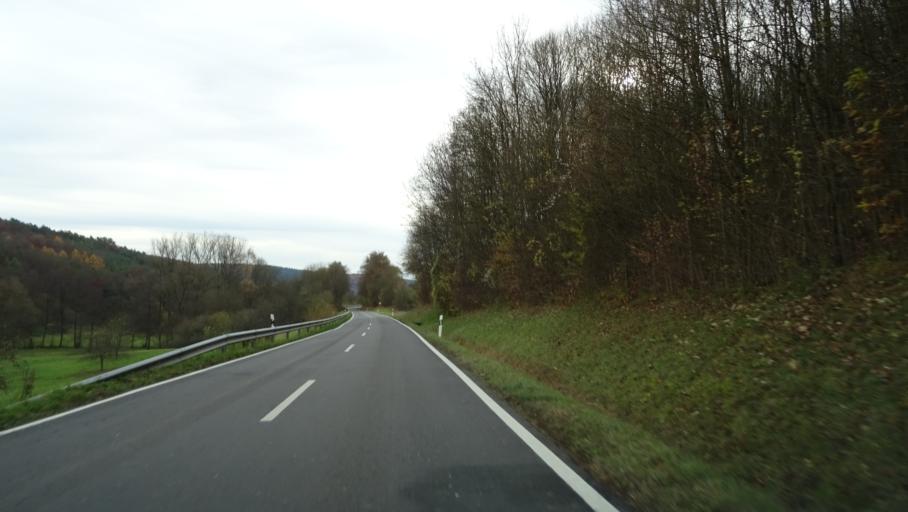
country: DE
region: Baden-Wuerttemberg
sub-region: Karlsruhe Region
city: Mosbach
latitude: 49.3648
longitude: 9.1265
